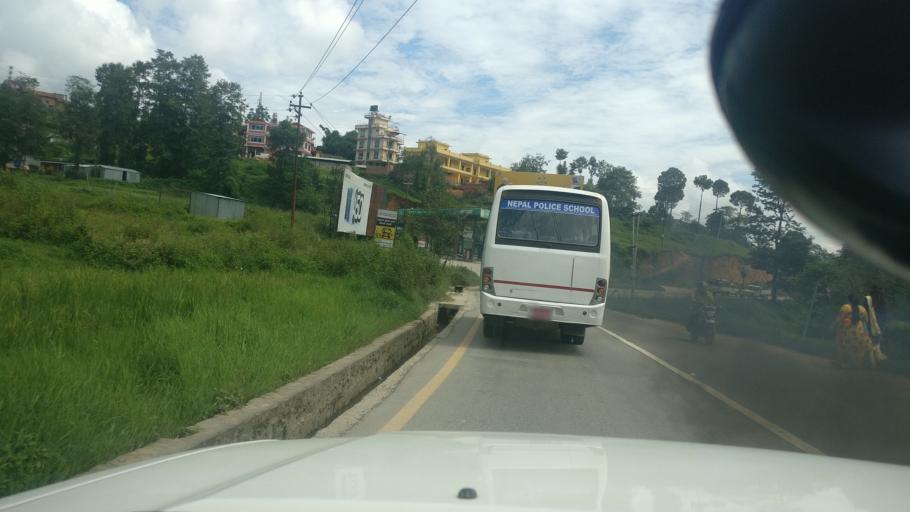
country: NP
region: Central Region
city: Banepa
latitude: 27.6318
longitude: 85.4979
